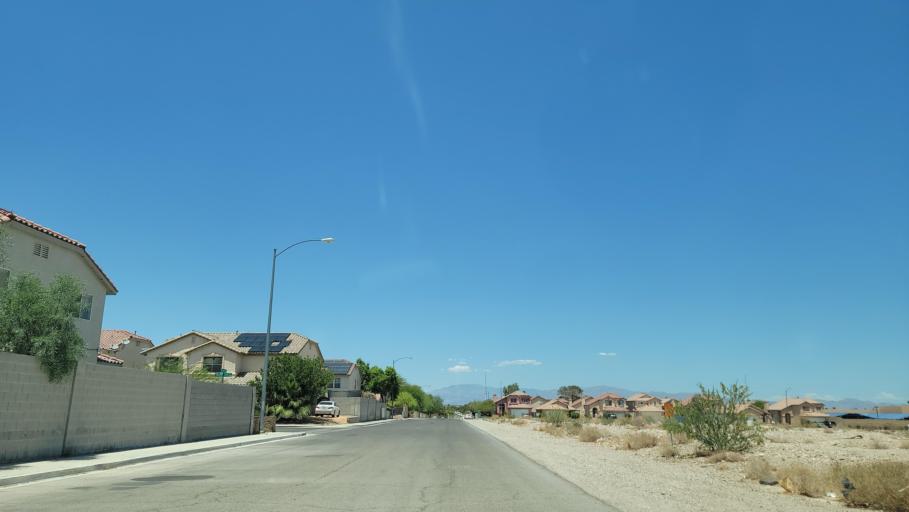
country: US
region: Nevada
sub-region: Clark County
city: Spring Valley
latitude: 36.0816
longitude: -115.2655
